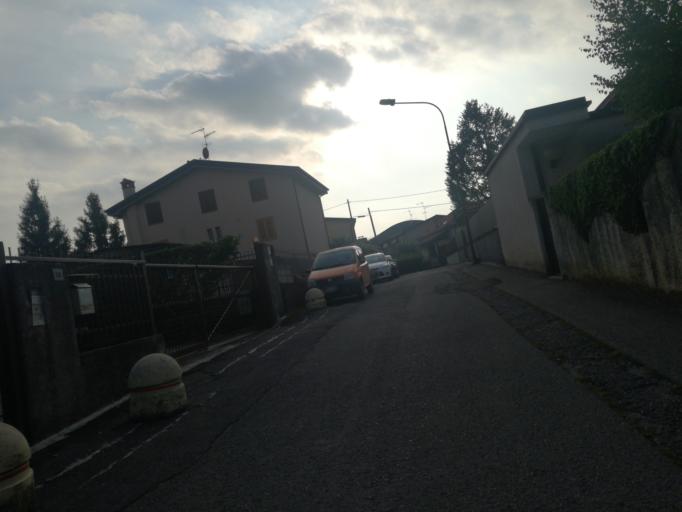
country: IT
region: Lombardy
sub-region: Provincia di Monza e Brianza
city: Porto d'Adda
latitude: 45.6527
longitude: 9.4641
